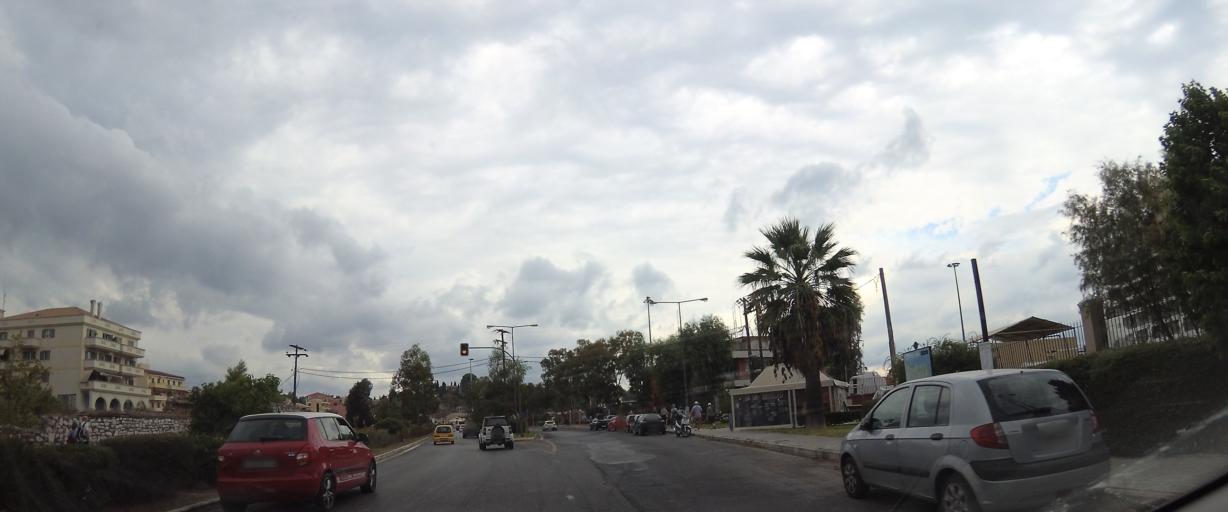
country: GR
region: Ionian Islands
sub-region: Nomos Kerkyras
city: Kerkyra
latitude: 39.6266
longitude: 19.9064
